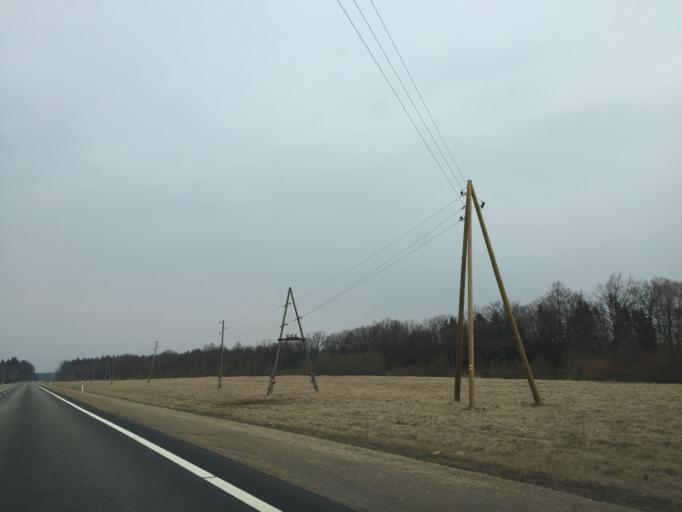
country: LV
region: Salacgrivas
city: Salacgriva
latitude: 57.7056
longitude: 24.3699
